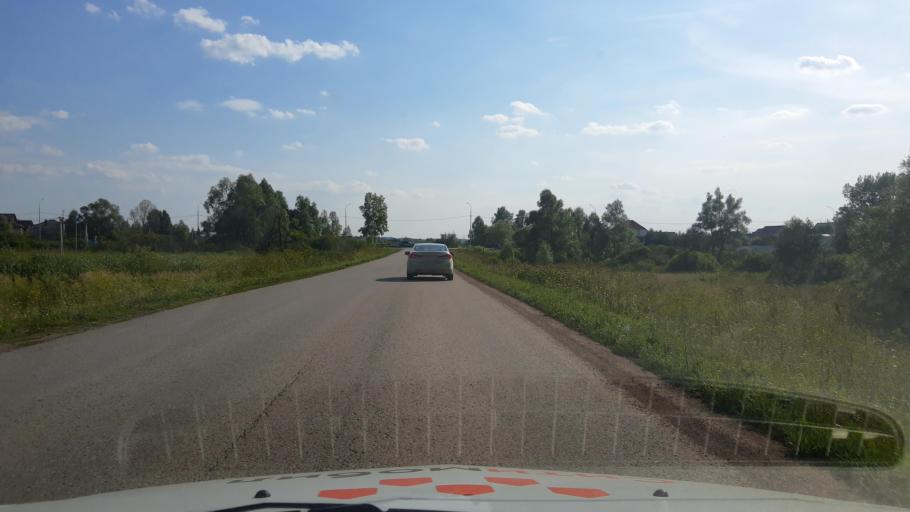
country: RU
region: Bashkortostan
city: Kabakovo
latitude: 54.6608
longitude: 56.1754
